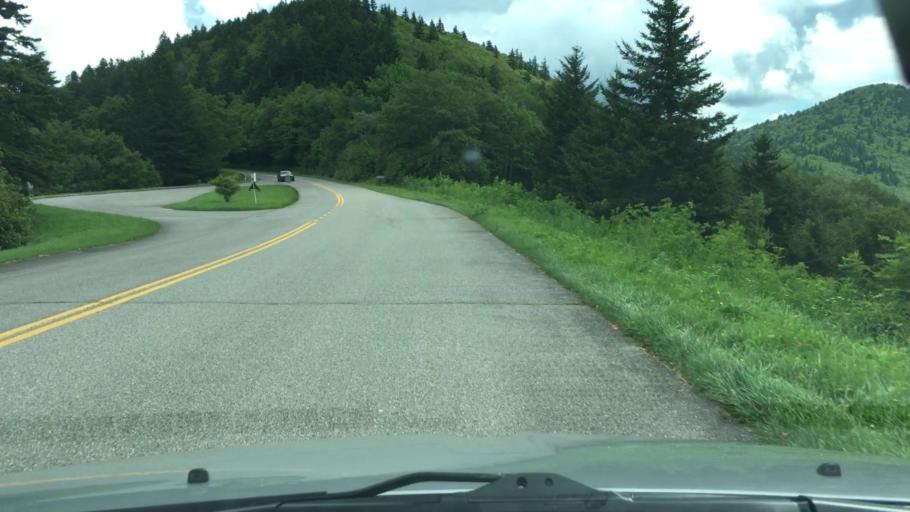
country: US
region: North Carolina
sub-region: Buncombe County
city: Black Mountain
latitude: 35.7175
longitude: -82.2793
